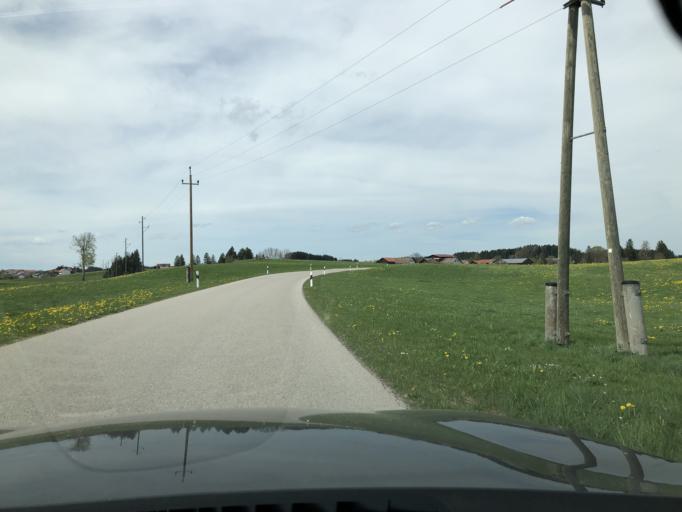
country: DE
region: Bavaria
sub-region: Swabia
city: Wald
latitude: 47.7036
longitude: 10.5648
